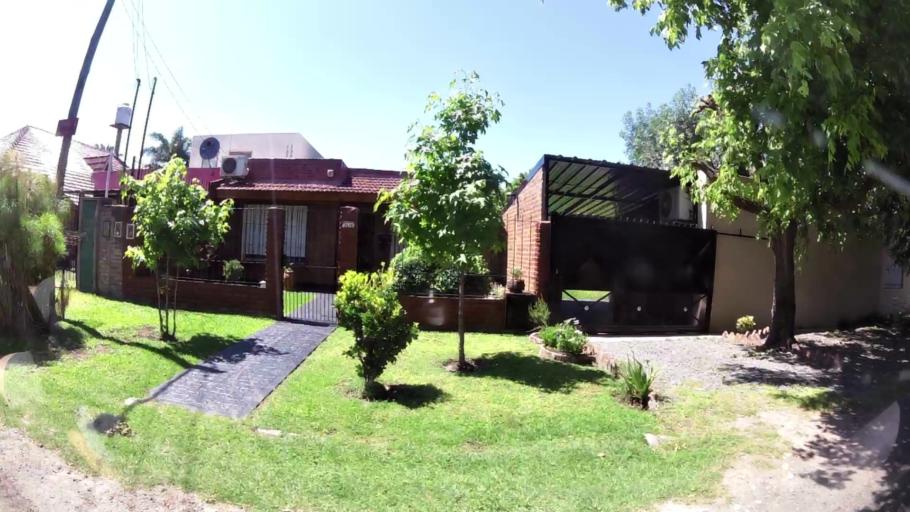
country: AR
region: Buenos Aires
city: Ituzaingo
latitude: -34.6805
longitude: -58.6734
